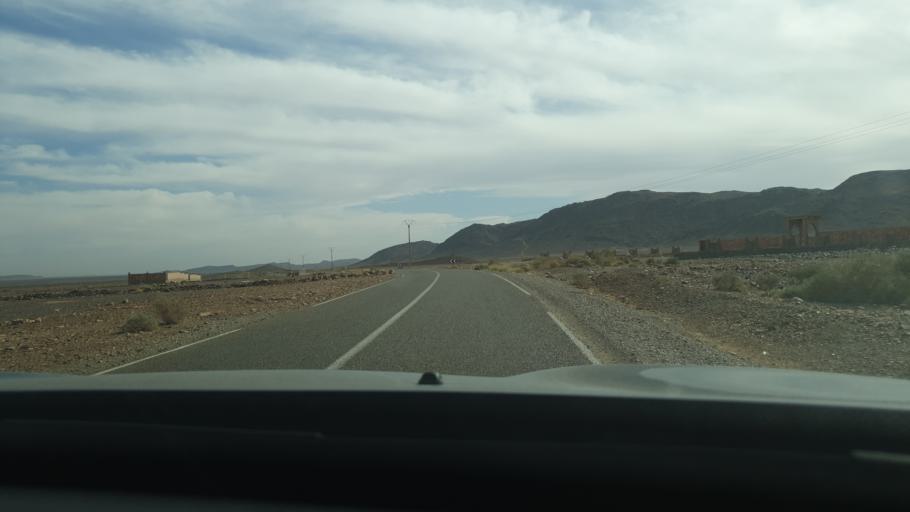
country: MA
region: Meknes-Tafilalet
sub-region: Errachidia
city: Fezna
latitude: 31.5290
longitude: -4.6375
